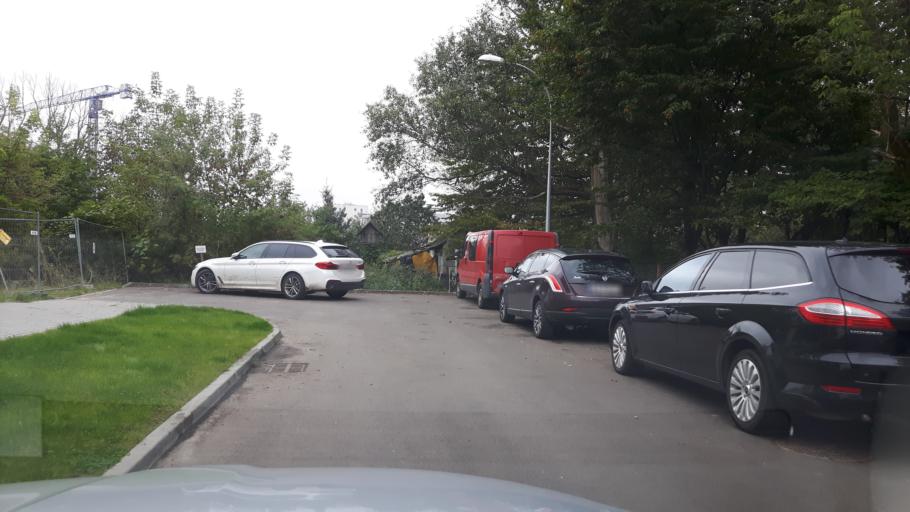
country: PL
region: Masovian Voivodeship
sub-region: Warszawa
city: Mokotow
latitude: 52.1778
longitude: 21.0381
